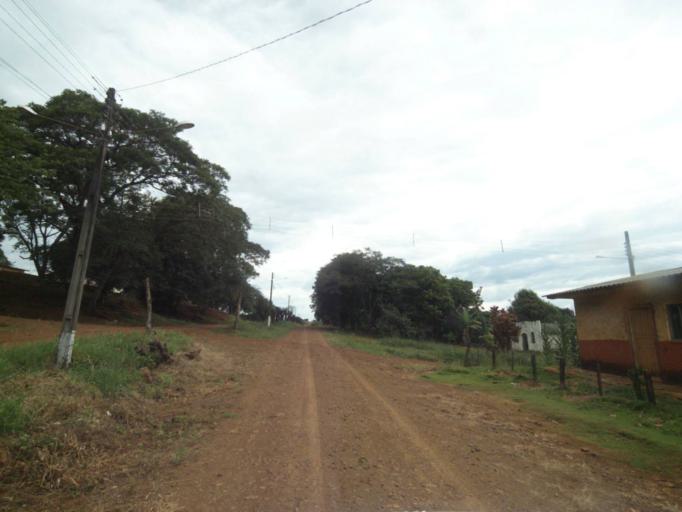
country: BR
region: Parana
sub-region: Guaraniacu
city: Guaraniacu
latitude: -24.9160
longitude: -52.9377
